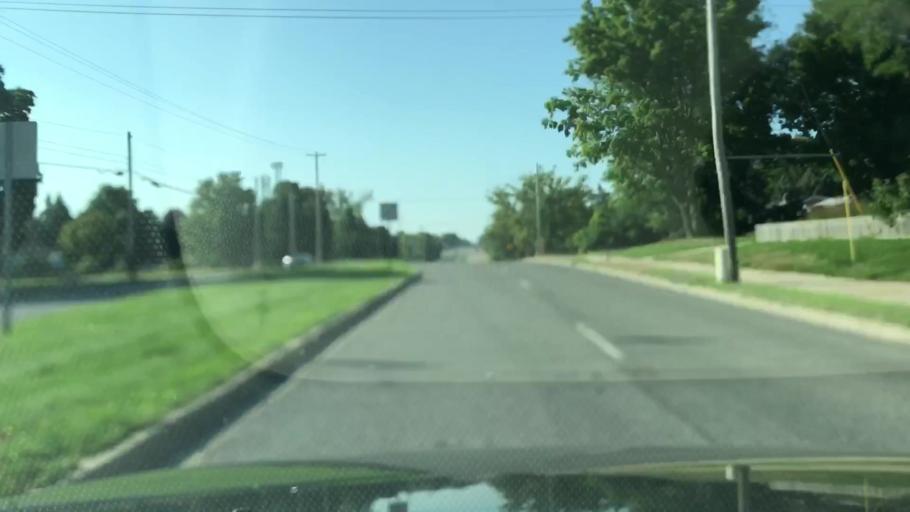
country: US
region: Michigan
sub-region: Kent County
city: Kentwood
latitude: 42.8753
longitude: -85.6257
